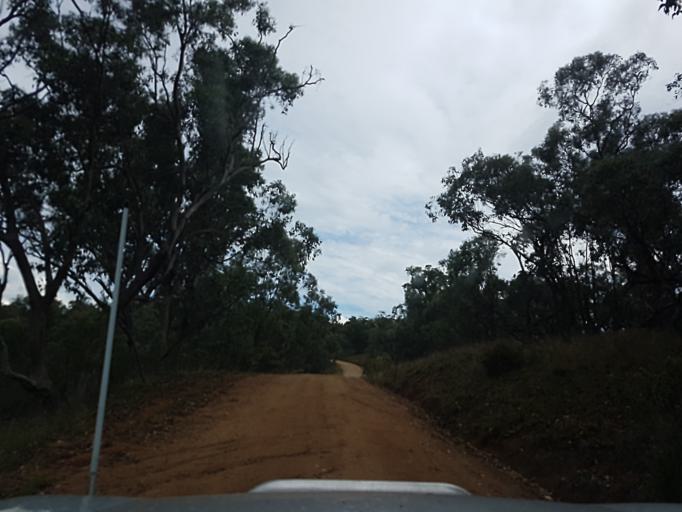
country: AU
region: New South Wales
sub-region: Snowy River
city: Jindabyne
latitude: -36.9419
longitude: 148.3460
